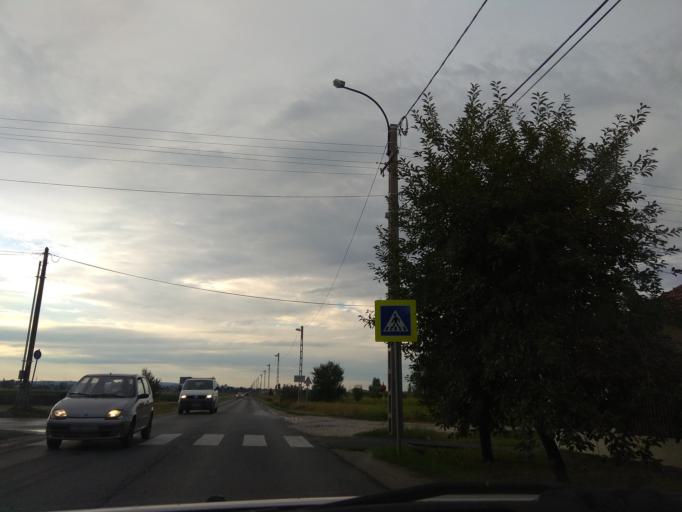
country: HU
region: Borsod-Abauj-Zemplen
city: Miskolc
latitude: 48.0774
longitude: 20.8239
